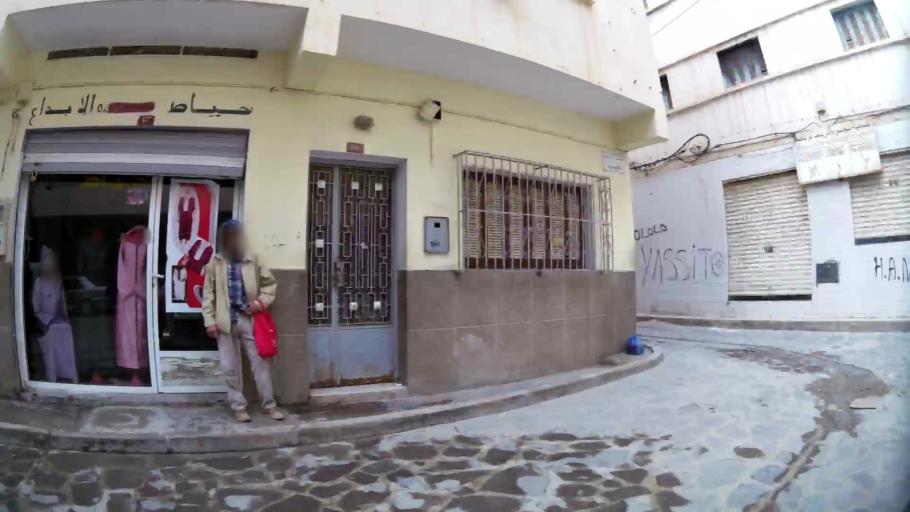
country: MA
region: Oriental
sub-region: Nador
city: Nador
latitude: 35.1698
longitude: -2.9295
